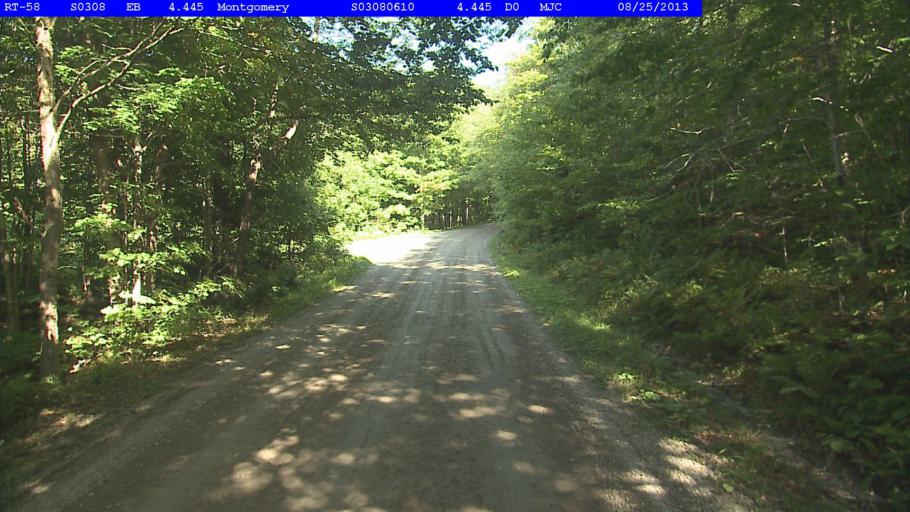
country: US
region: Vermont
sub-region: Franklin County
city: Richford
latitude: 44.8441
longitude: -72.5389
